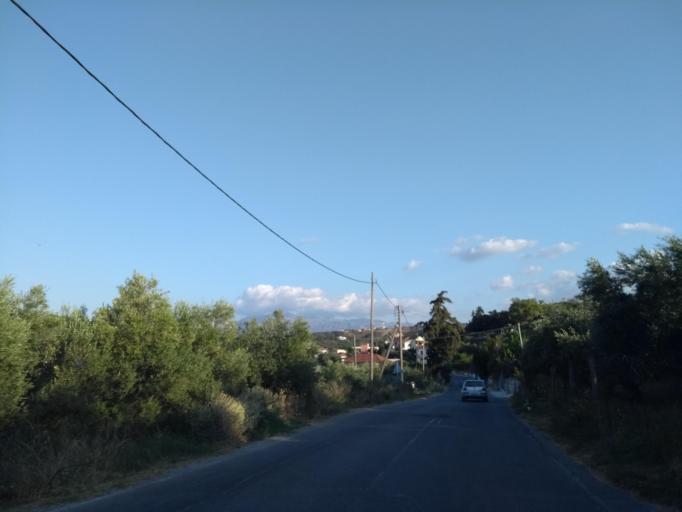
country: GR
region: Crete
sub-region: Nomos Chanias
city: Kalivai
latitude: 35.4364
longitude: 24.1790
